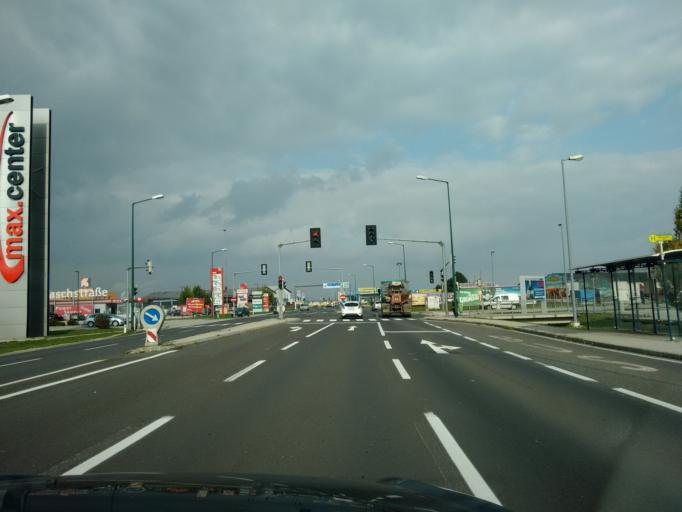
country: AT
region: Upper Austria
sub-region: Wels-Land
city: Gunskirchen
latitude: 48.1459
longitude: 13.9743
